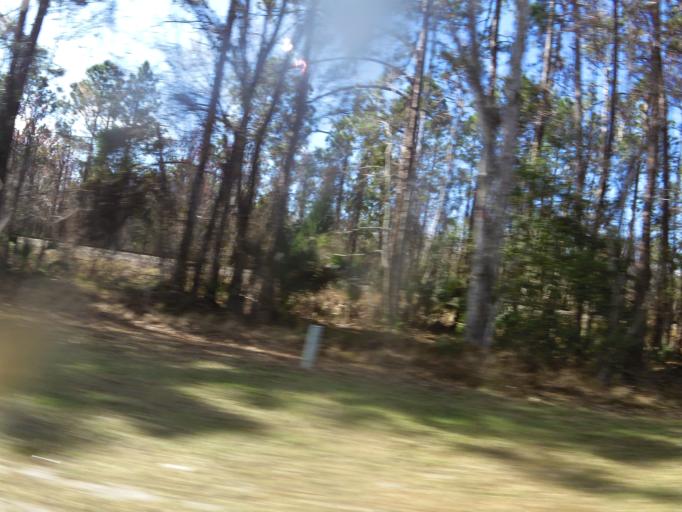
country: US
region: Florida
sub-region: Volusia County
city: Pierson
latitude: 29.2867
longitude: -81.4790
